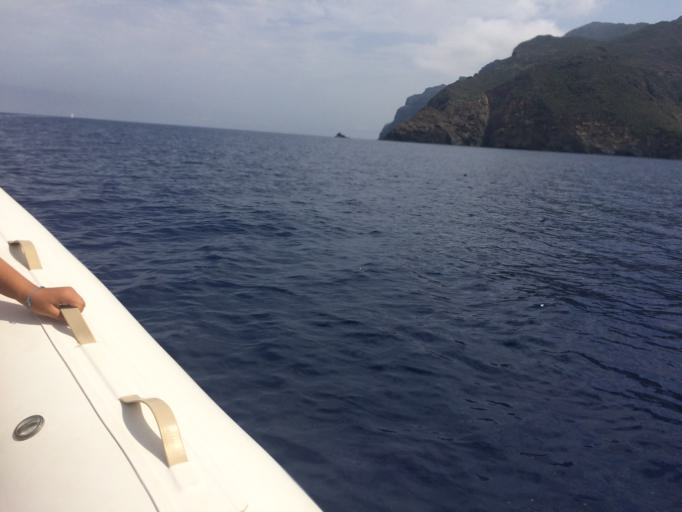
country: IT
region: Tuscany
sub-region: Provincia di Livorno
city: Capraia Isola
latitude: 43.0485
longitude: 9.7935
